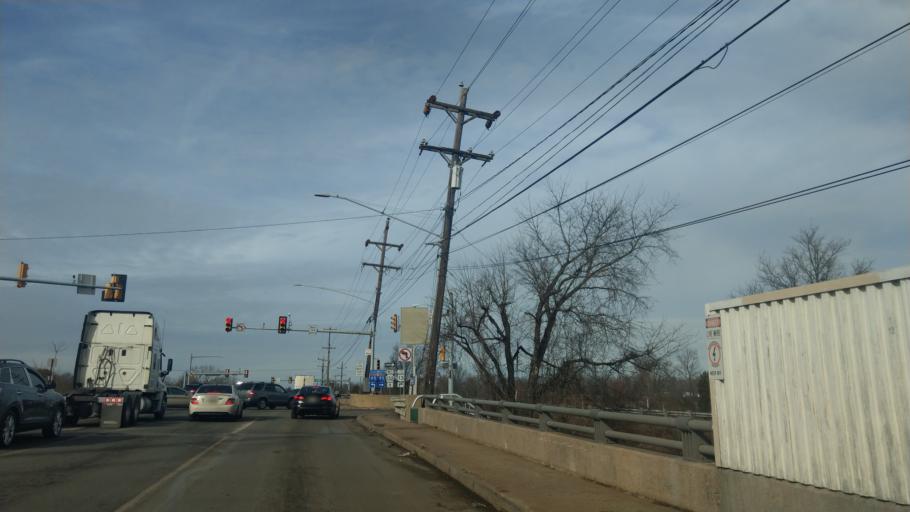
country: US
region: Pennsylvania
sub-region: Bucks County
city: Eddington
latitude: 40.0828
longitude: -74.9340
